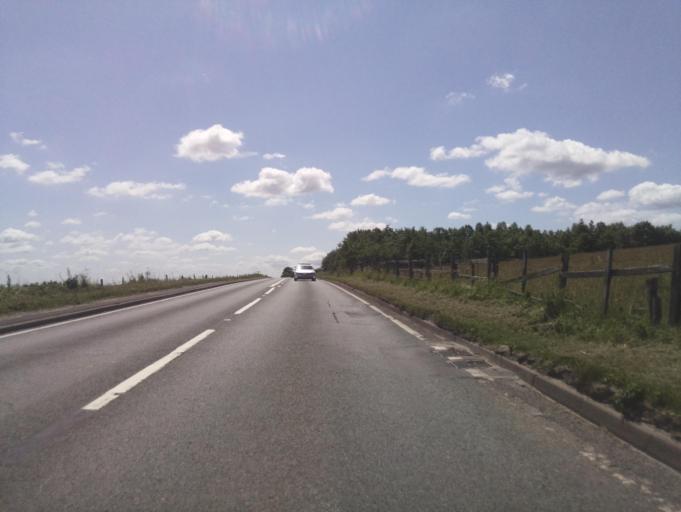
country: GB
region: England
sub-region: Derbyshire
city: Buxton
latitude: 53.2881
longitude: -1.8894
